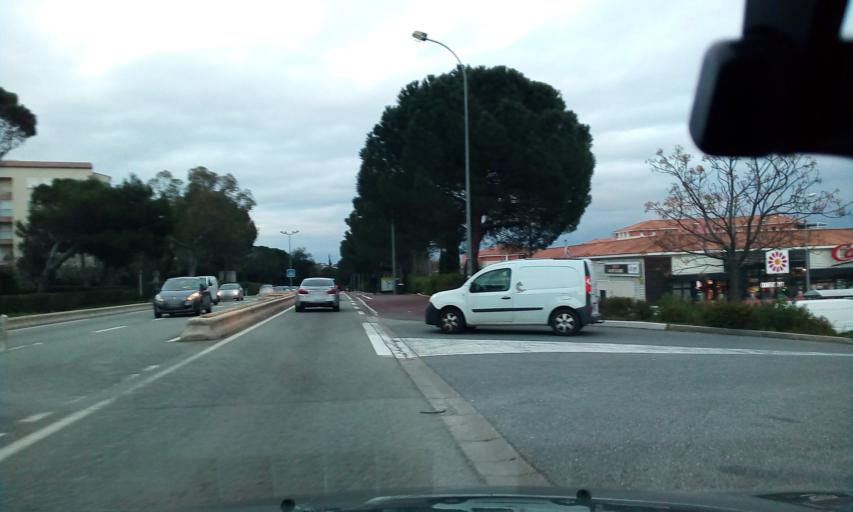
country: FR
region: Provence-Alpes-Cote d'Azur
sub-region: Departement du Var
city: Frejus
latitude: 43.4395
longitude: 6.7452
